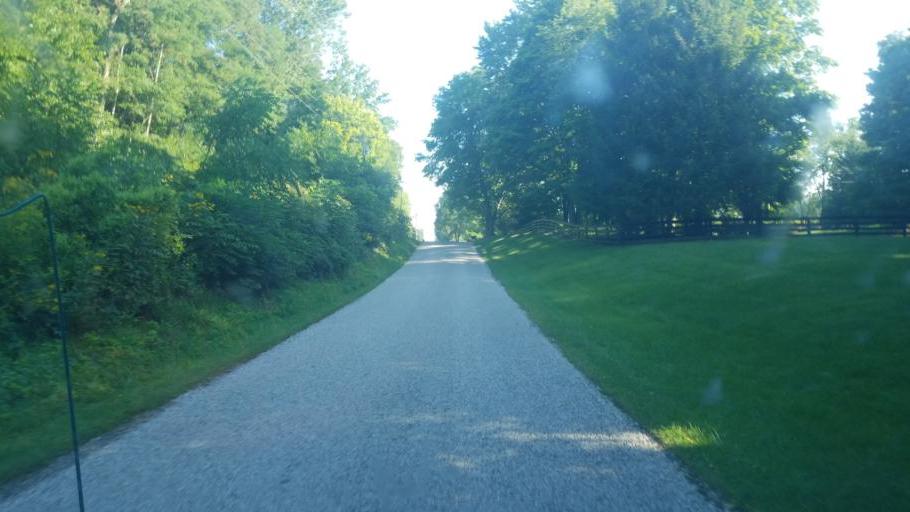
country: US
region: Ohio
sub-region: Ashland County
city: Ashland
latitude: 40.9425
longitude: -82.3397
